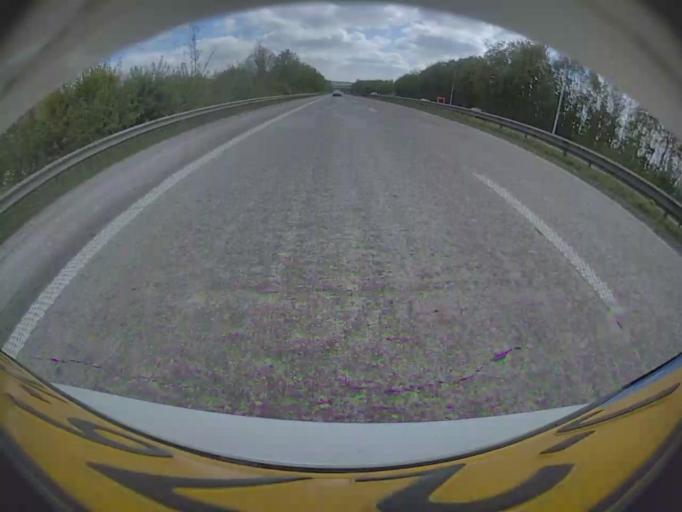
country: BE
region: Wallonia
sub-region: Province de Namur
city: Houyet
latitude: 50.2227
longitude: 5.0599
